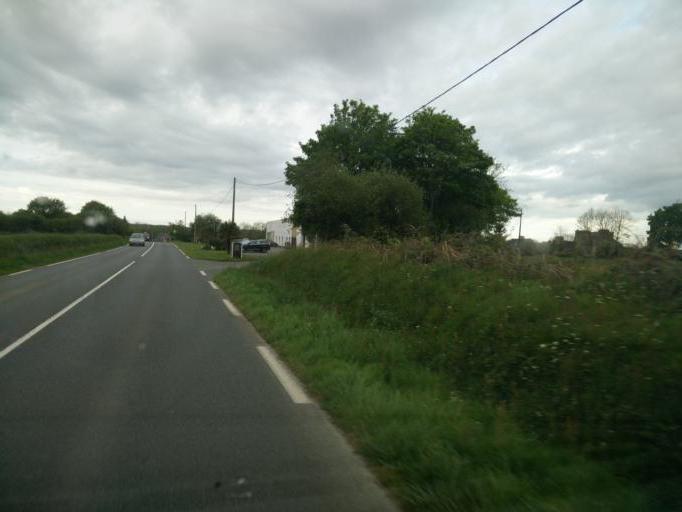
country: FR
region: Brittany
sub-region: Departement des Cotes-d'Armor
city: Lannion
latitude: 48.7140
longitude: -3.4968
